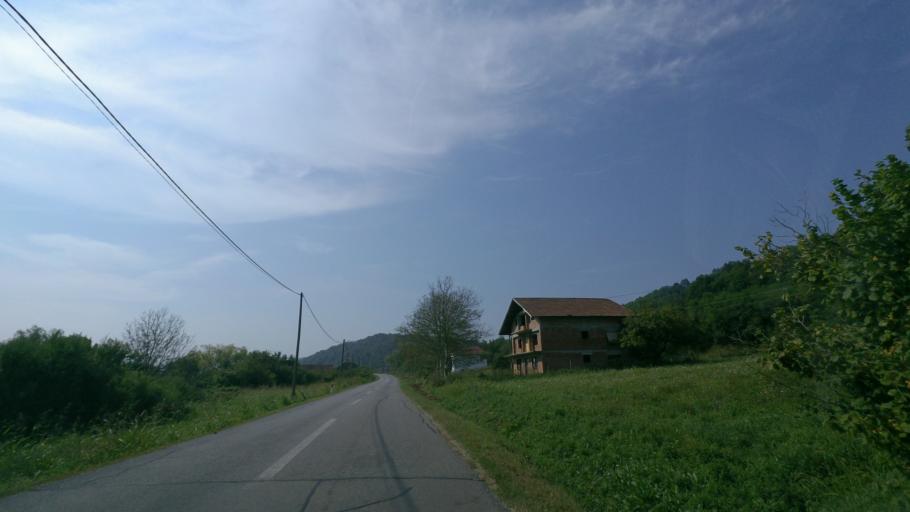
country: BA
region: Republika Srpska
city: Dobrljin
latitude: 45.1815
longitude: 16.4728
